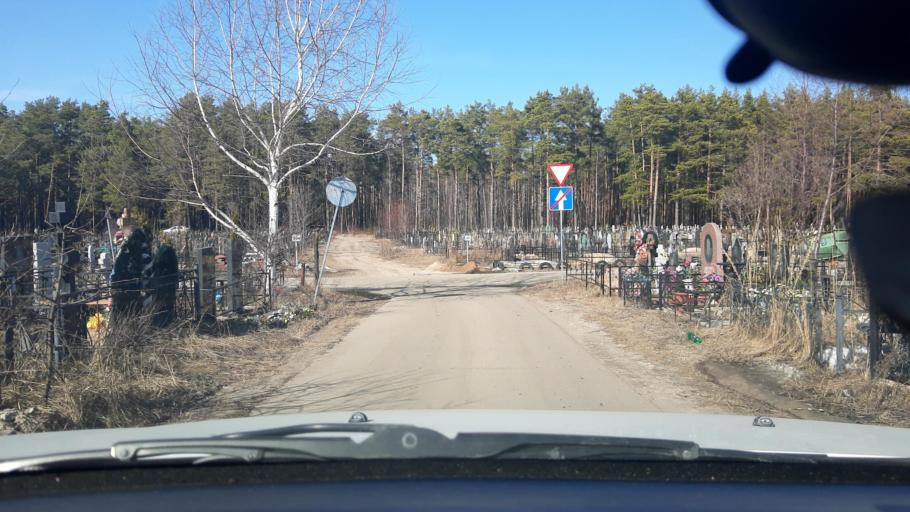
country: RU
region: Nizjnij Novgorod
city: Pyra
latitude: 56.2433
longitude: 43.3707
